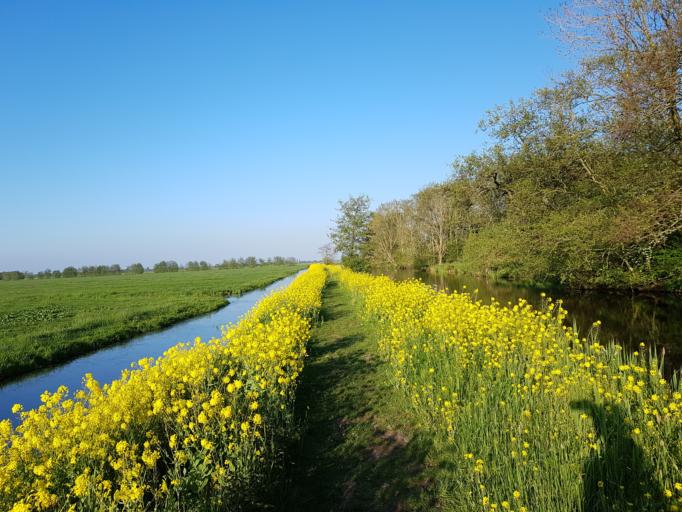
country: NL
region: South Holland
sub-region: Gemeente Vlist
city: Vlist
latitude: 51.9561
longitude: 4.8037
